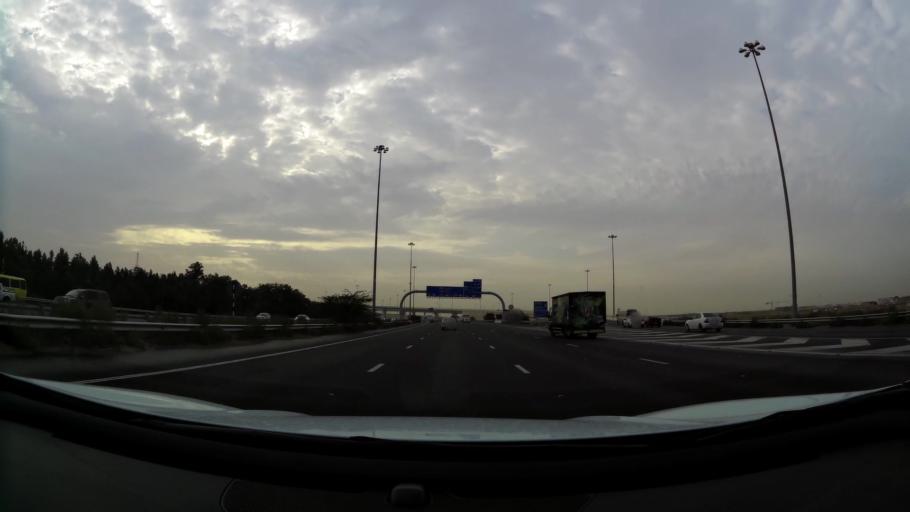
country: AE
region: Abu Dhabi
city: Abu Dhabi
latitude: 24.3152
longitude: 54.5942
